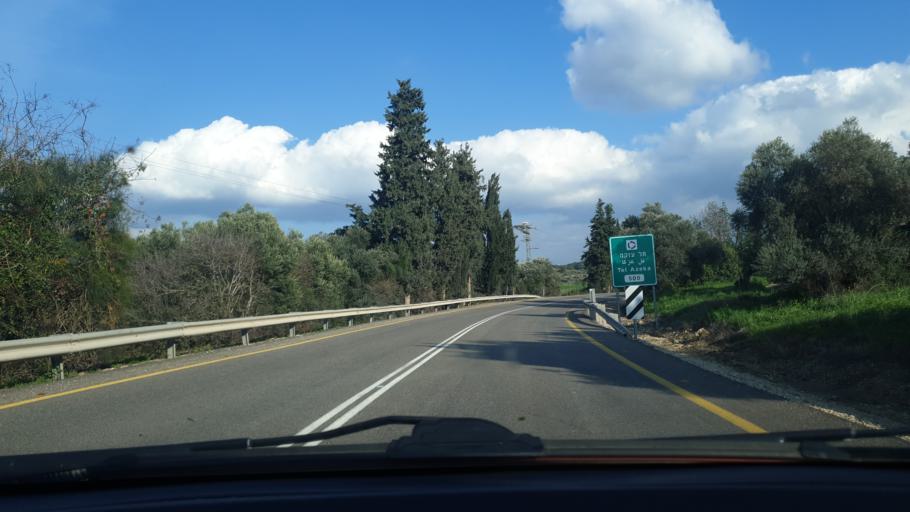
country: IL
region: Jerusalem
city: Bet Shemesh
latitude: 31.7043
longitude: 34.9377
